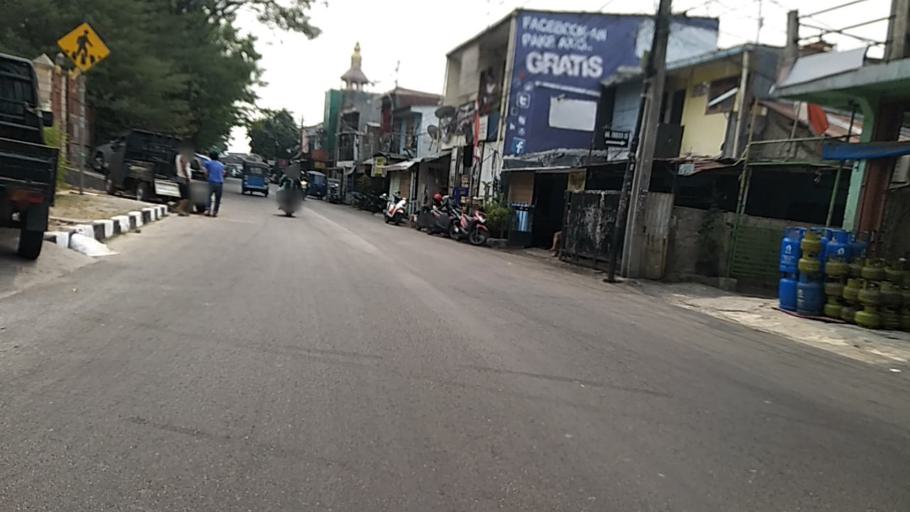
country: ID
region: Jakarta Raya
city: Jakarta
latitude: -6.2319
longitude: 106.8514
